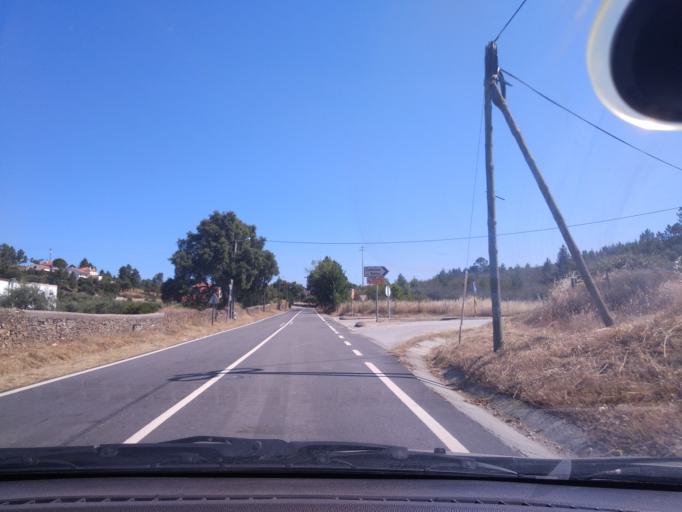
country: PT
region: Castelo Branco
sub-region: Castelo Branco
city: Castelo Branco
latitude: 39.7442
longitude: -7.6209
